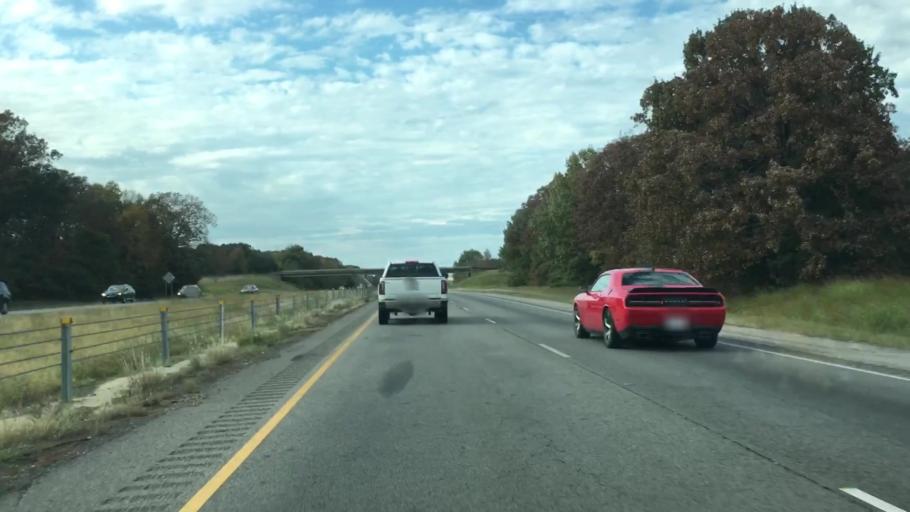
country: US
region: Arkansas
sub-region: Conway County
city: Morrilton
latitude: 35.2177
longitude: -92.8276
